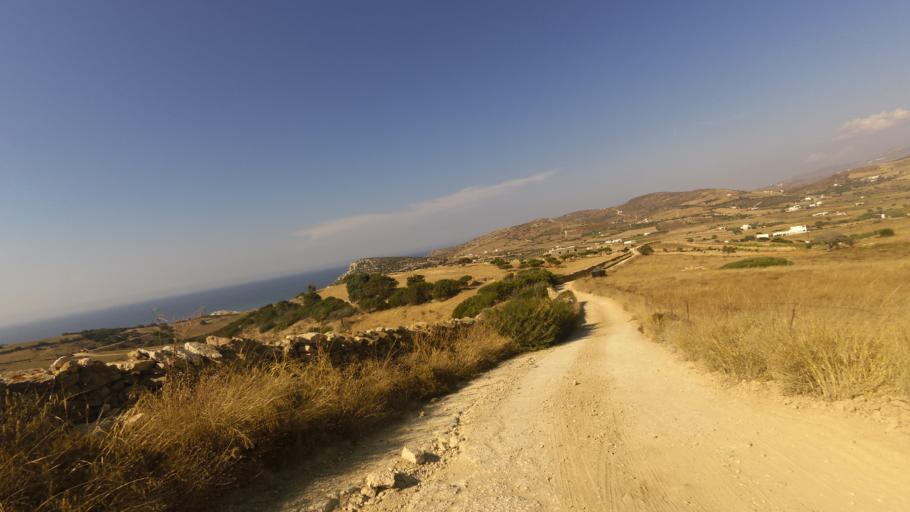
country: GR
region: South Aegean
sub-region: Nomos Kykladon
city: Antiparos
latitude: 37.0104
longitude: 25.0462
